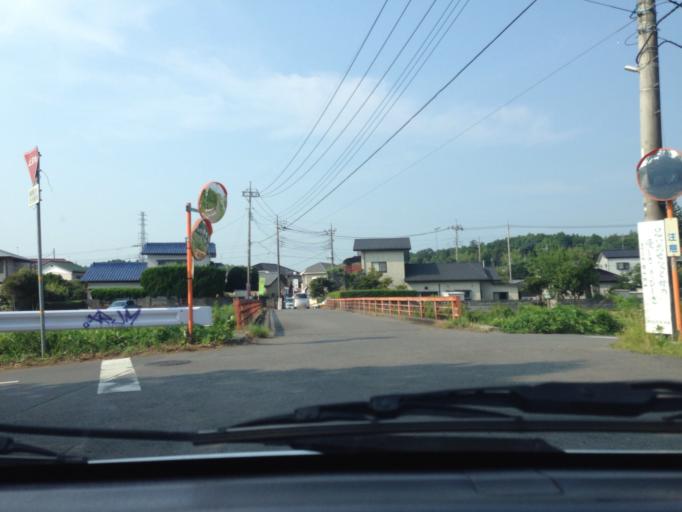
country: JP
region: Ibaraki
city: Ami
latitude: 36.0510
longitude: 140.2151
